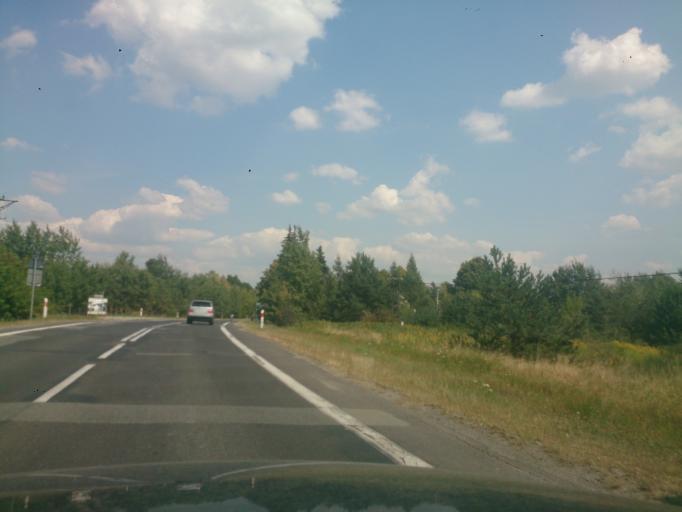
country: PL
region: Subcarpathian Voivodeship
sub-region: Powiat kolbuszowski
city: Majdan Krolewski
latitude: 50.3664
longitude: 21.7349
